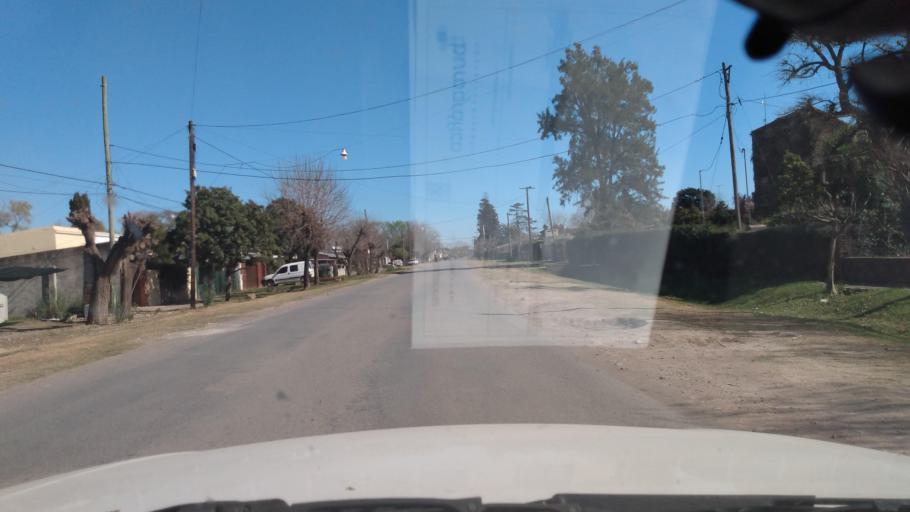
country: AR
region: Buenos Aires
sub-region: Partido de Mercedes
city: Mercedes
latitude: -34.6582
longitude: -59.4057
